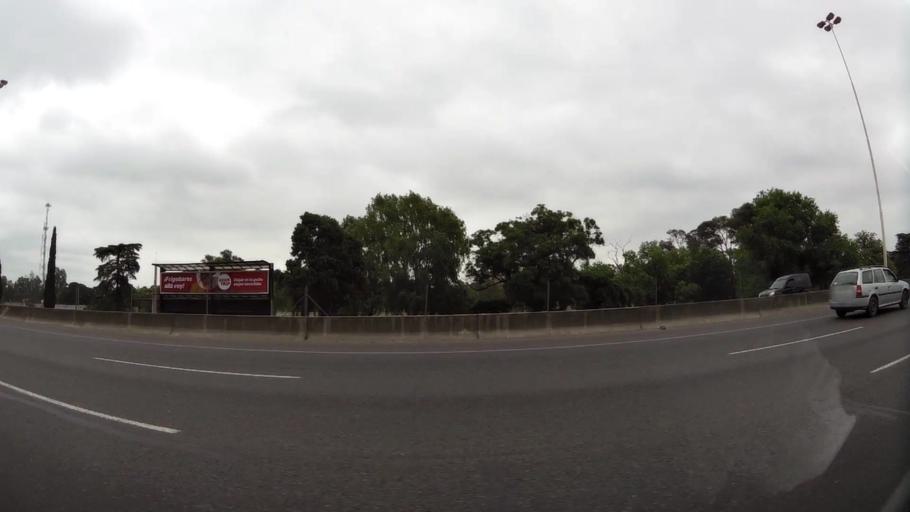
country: AR
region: Buenos Aires
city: San Justo
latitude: -34.7438
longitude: -58.5211
